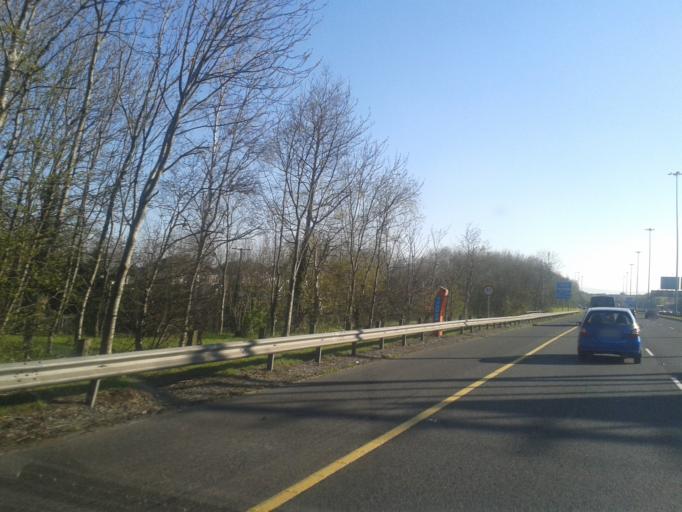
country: IE
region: Leinster
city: Beaumont
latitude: 53.4034
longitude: -6.2325
